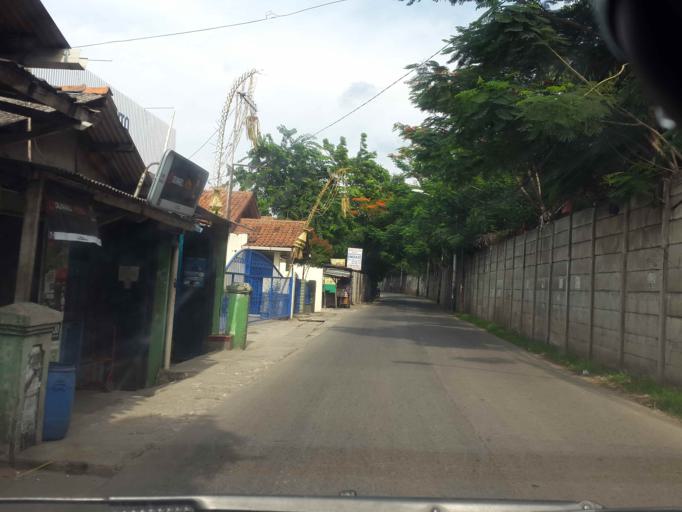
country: ID
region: Banten
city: Tangerang
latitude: -6.2234
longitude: 106.6426
